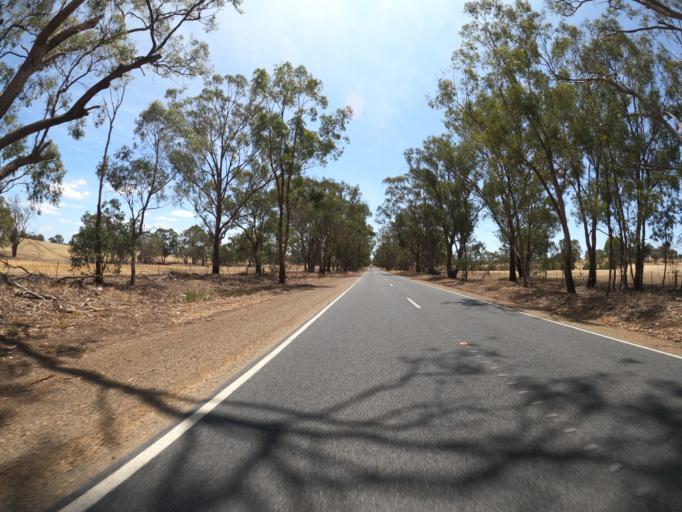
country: AU
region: Victoria
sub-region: Benalla
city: Benalla
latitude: -36.3670
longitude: 145.9705
